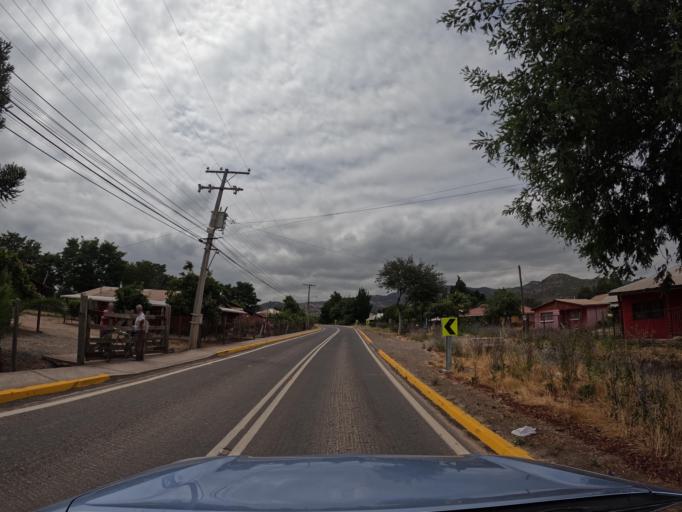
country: CL
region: Maule
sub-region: Provincia de Curico
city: Teno
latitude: -34.7748
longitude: -71.1838
